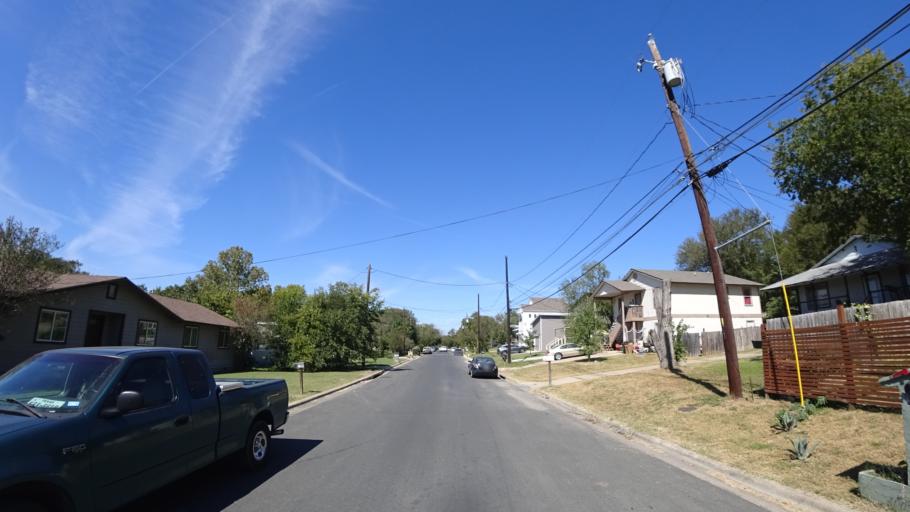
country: US
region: Texas
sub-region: Travis County
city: Austin
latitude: 30.2740
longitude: -97.6793
